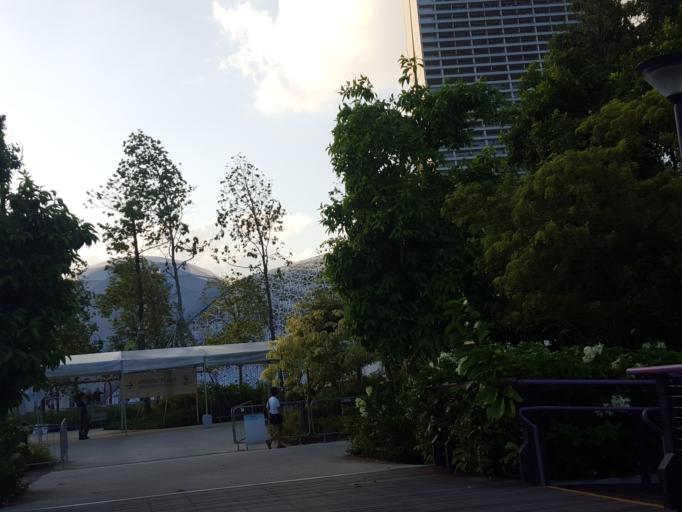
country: SG
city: Singapore
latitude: 1.2808
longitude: 103.8616
